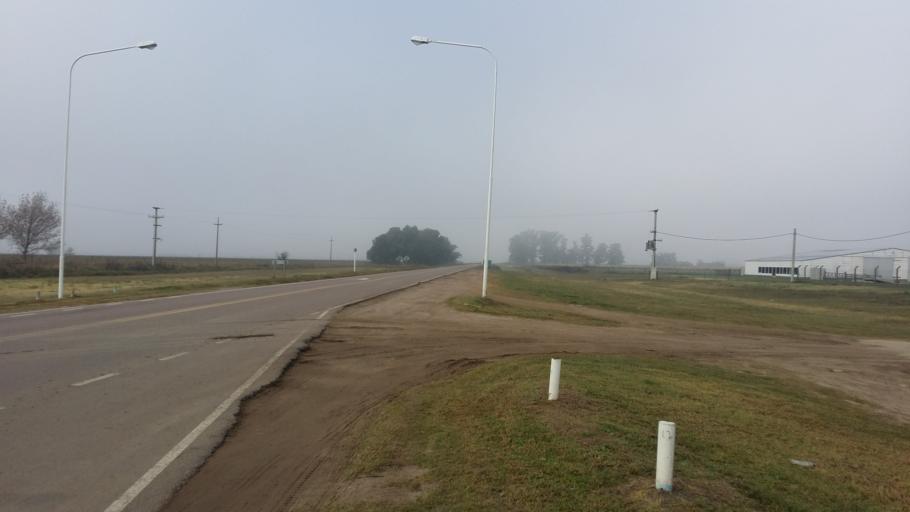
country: AR
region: La Pampa
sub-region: Departamento de Quemu Quemu
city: Quemu Quemu
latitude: -36.0649
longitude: -63.5844
